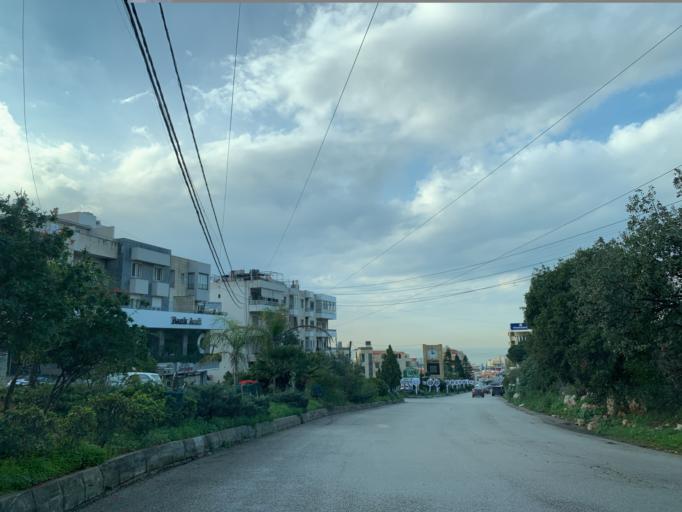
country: LB
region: Mont-Liban
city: Jdaidet el Matn
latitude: 33.8538
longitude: 35.5777
